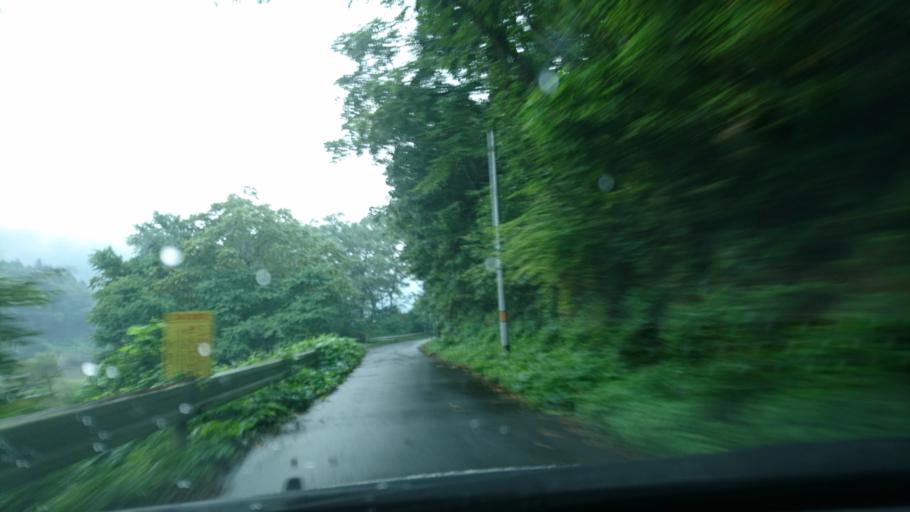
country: JP
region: Iwate
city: Ichinoseki
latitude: 38.8776
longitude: 141.2587
